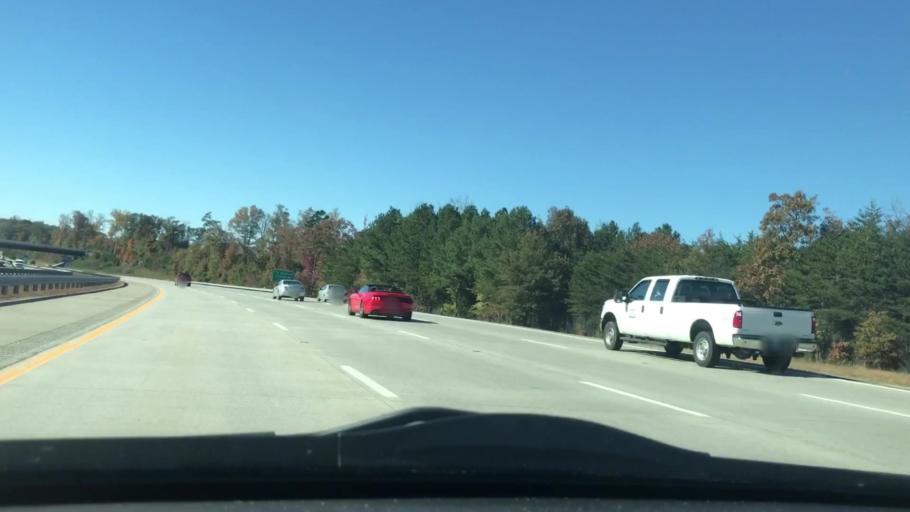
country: US
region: North Carolina
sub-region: Guilford County
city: Jamestown
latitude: 36.0444
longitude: -79.8975
